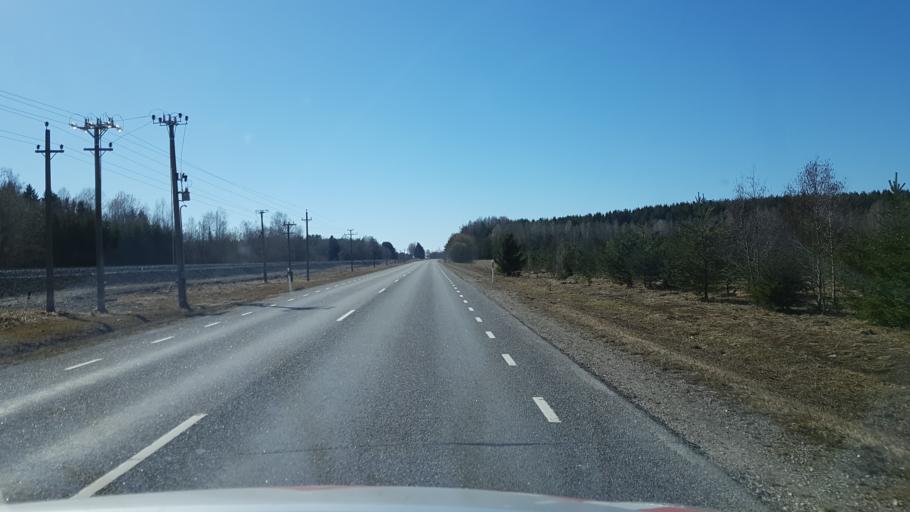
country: EE
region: Ida-Virumaa
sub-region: Aseri vald
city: Aseri
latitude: 59.3480
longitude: 26.7839
